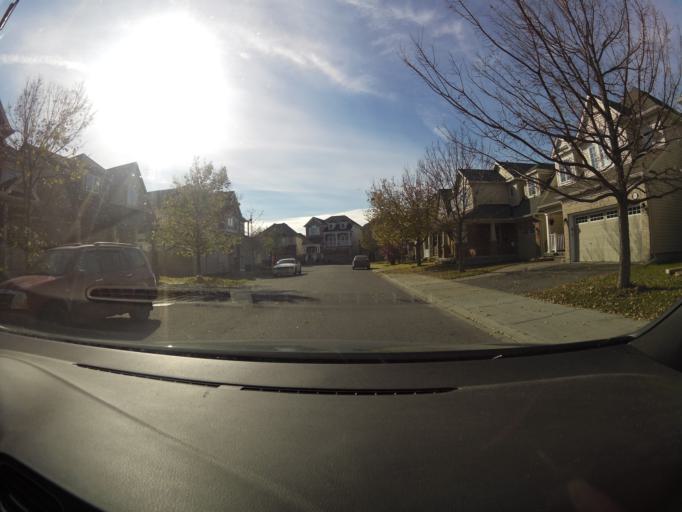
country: CA
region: Ontario
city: Bells Corners
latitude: 45.2899
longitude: -75.9162
